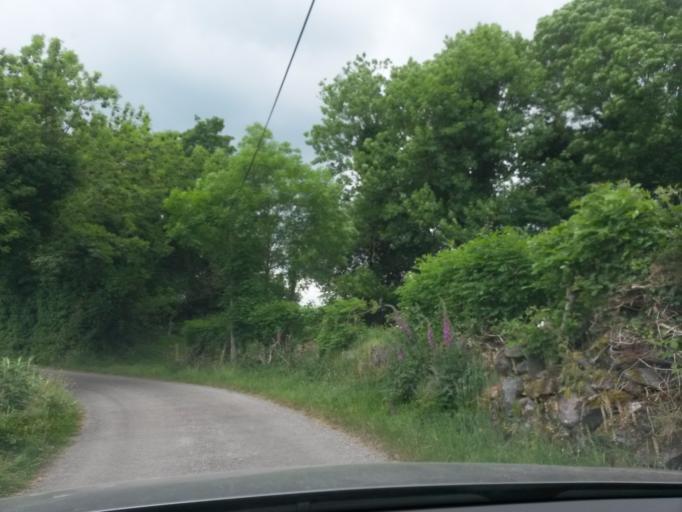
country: IE
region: Munster
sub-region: Ciarrai
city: Kenmare
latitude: 51.8234
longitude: -9.5150
